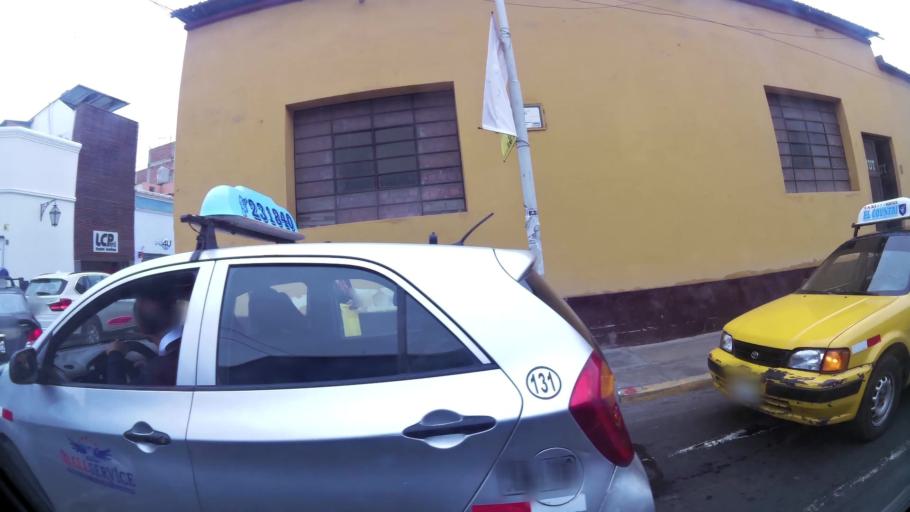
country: PE
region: La Libertad
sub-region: Provincia de Trujillo
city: Trujillo
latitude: -8.1111
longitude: -79.0305
